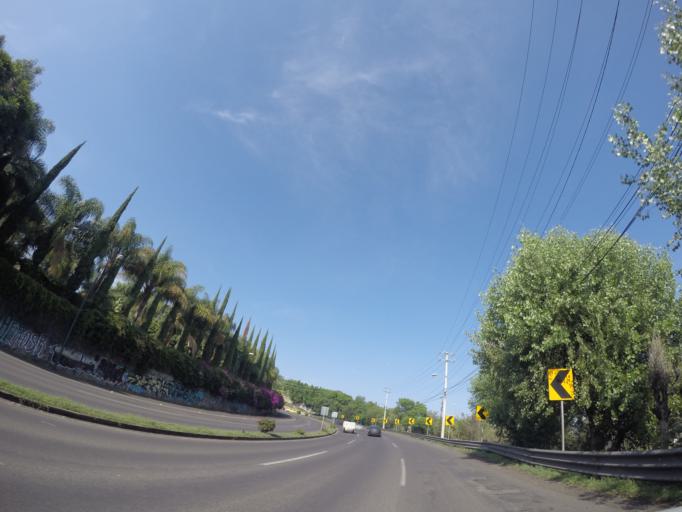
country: MX
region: Michoacan
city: Morelia
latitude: 19.6793
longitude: -101.1991
